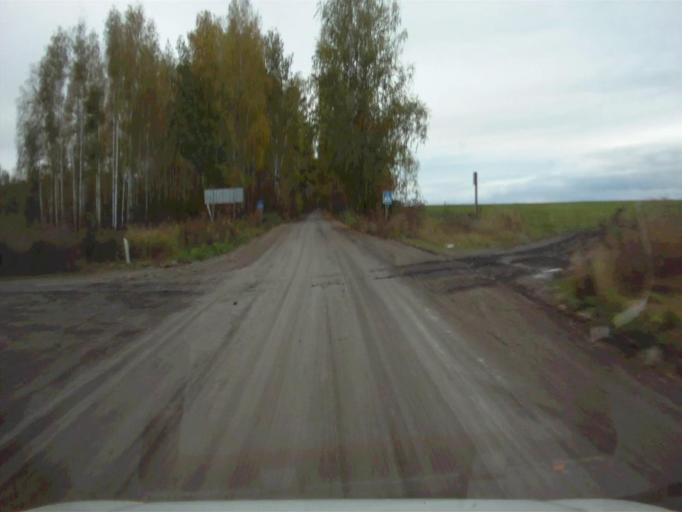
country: RU
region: Sverdlovsk
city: Mikhaylovsk
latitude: 56.1691
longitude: 59.2271
